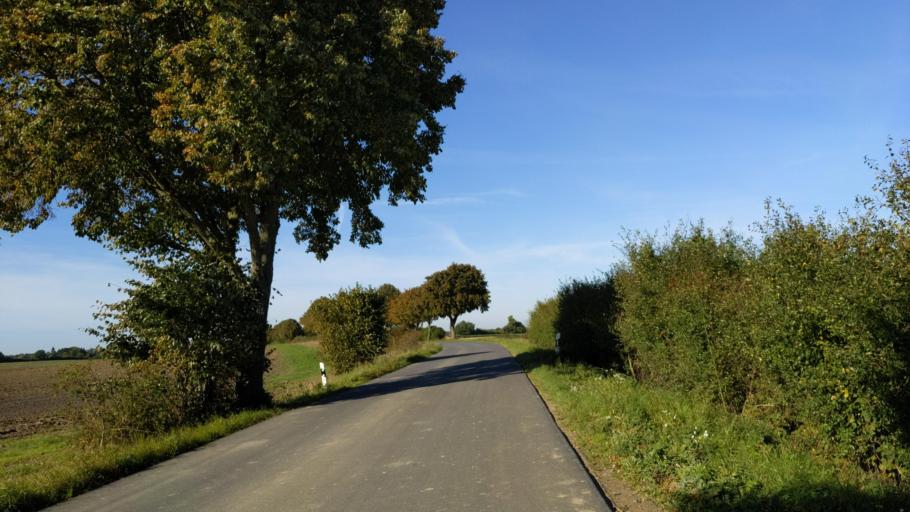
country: DE
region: Schleswig-Holstein
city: Ahrensbok
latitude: 54.0268
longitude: 10.6164
